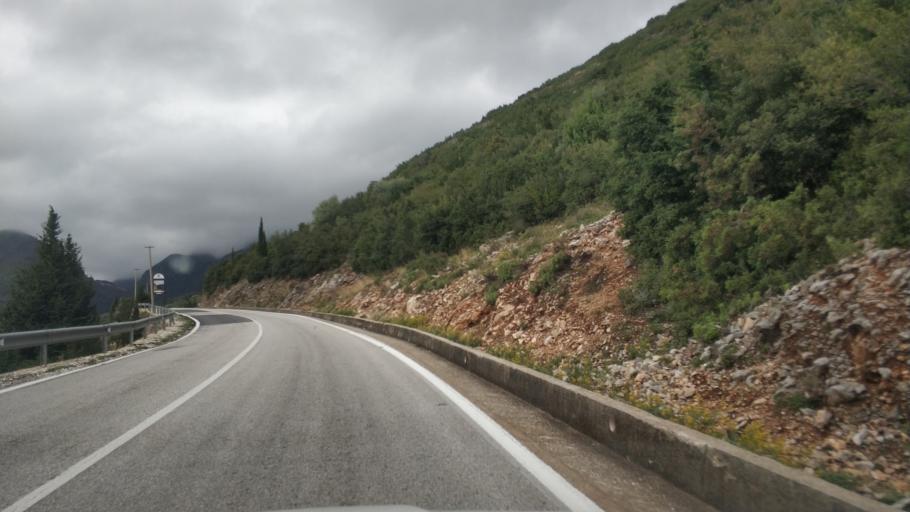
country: AL
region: Vlore
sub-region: Rrethi i Vlores
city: Vranisht
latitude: 40.1440
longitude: 19.6863
